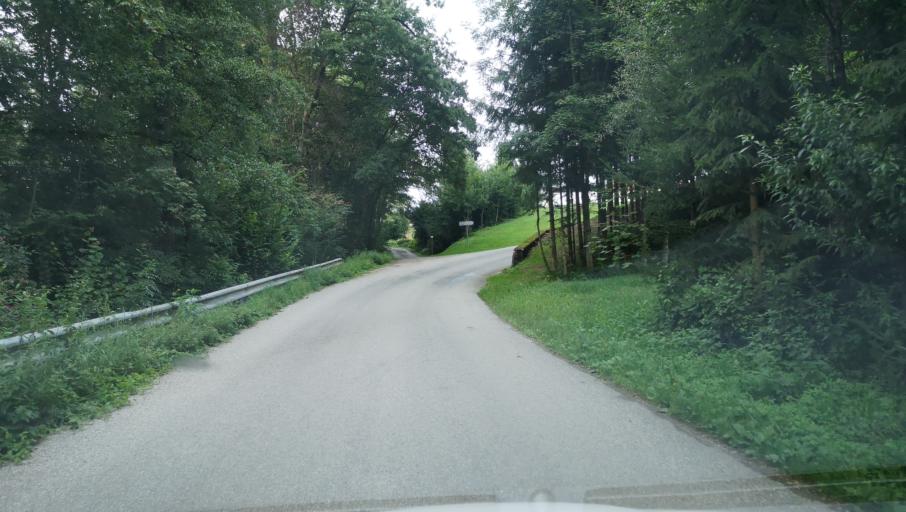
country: AT
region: Lower Austria
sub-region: Politischer Bezirk Amstetten
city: Zeillern
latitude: 48.1650
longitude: 14.8190
